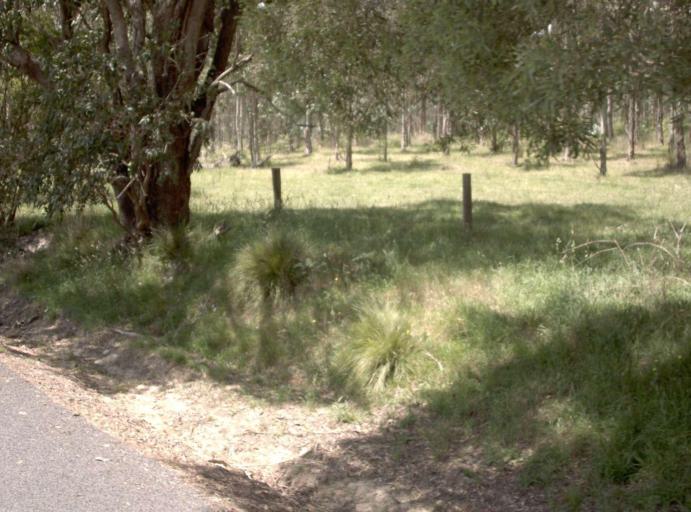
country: AU
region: New South Wales
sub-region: Bombala
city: Bombala
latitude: -37.4058
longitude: 149.0110
